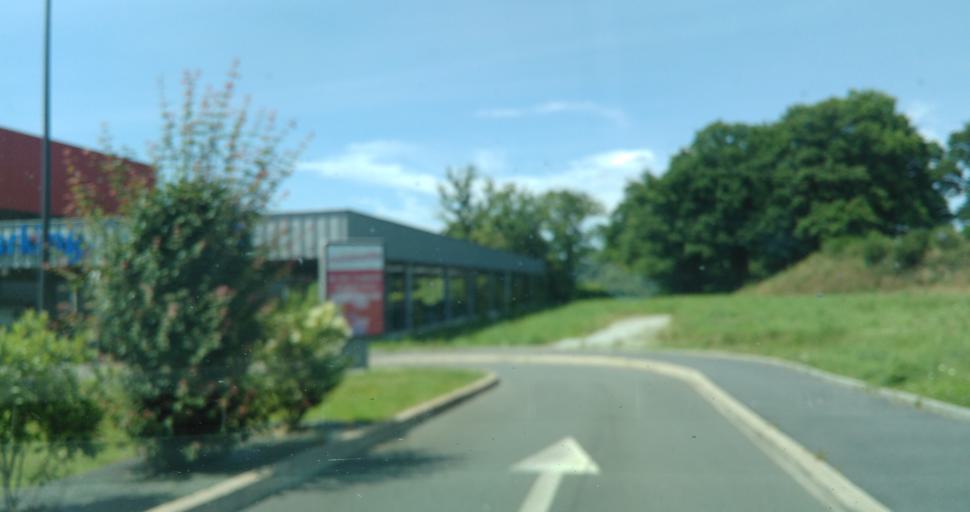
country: FR
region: Brittany
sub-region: Departement d'Ille-et-Vilaine
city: Chatillon-sur-Seiche
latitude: 48.0446
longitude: -1.6667
